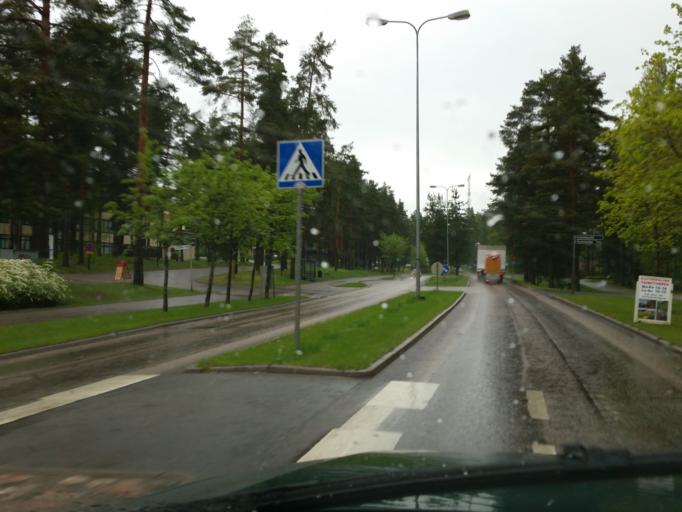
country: FI
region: Uusimaa
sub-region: Helsinki
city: Vihti
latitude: 60.3403
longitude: 24.3214
